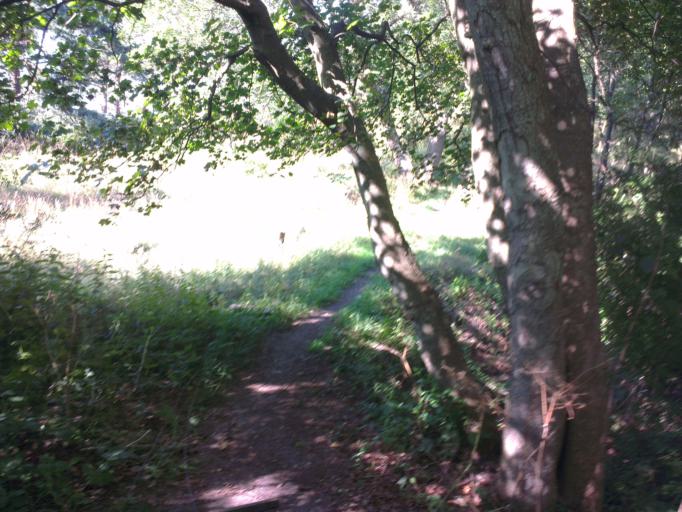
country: DK
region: Capital Region
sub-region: Frederikssund Kommune
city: Skibby
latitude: 55.7718
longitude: 12.0280
